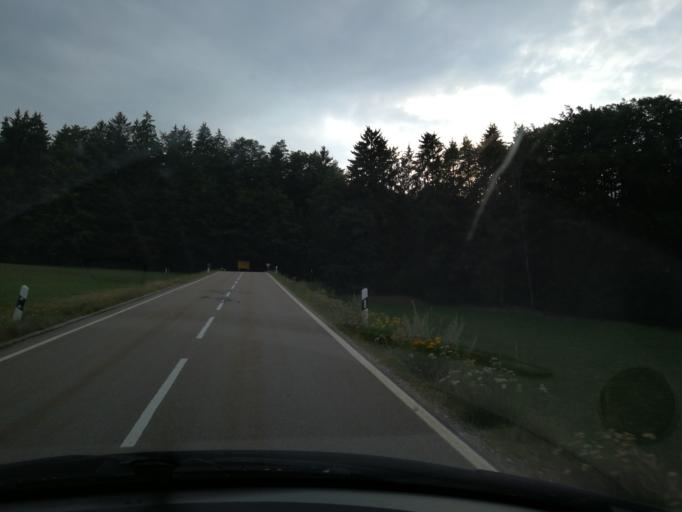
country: DE
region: Bavaria
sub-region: Lower Bavaria
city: Falkenfels
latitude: 49.0439
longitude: 12.5988
